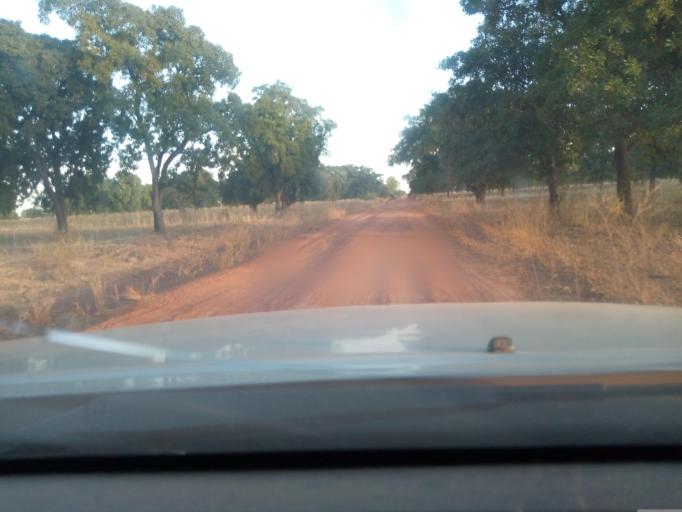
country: ML
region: Koulikoro
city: Dioila
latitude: 12.2072
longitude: -6.1977
